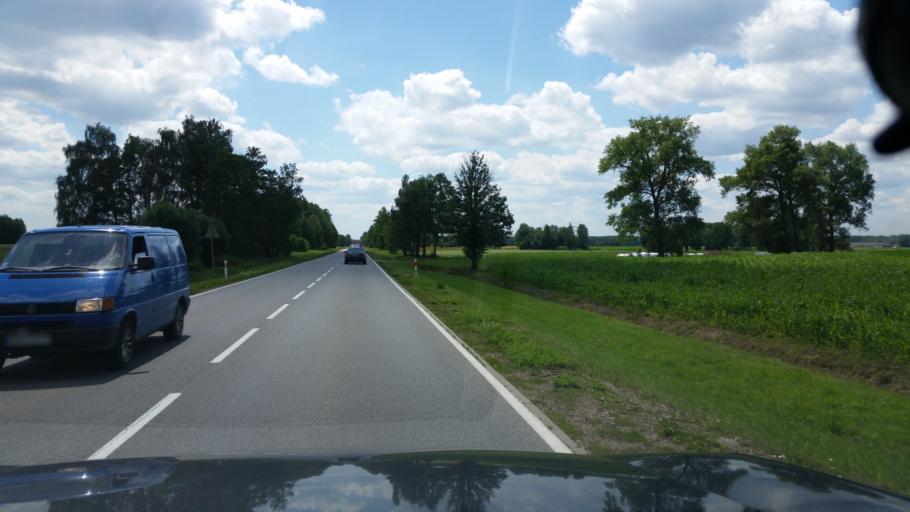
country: PL
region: Masovian Voivodeship
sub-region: Powiat ostrowski
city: Ostrow Mazowiecka
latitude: 52.9239
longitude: 21.8793
